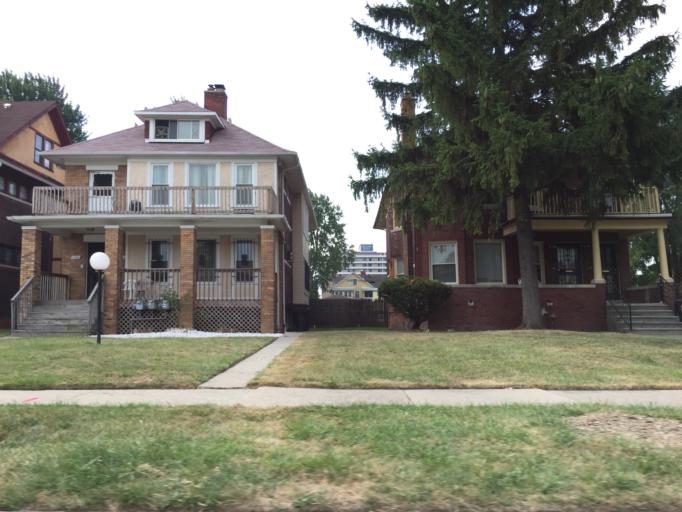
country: US
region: Michigan
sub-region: Wayne County
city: Highland Park
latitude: 42.3724
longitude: -83.0876
